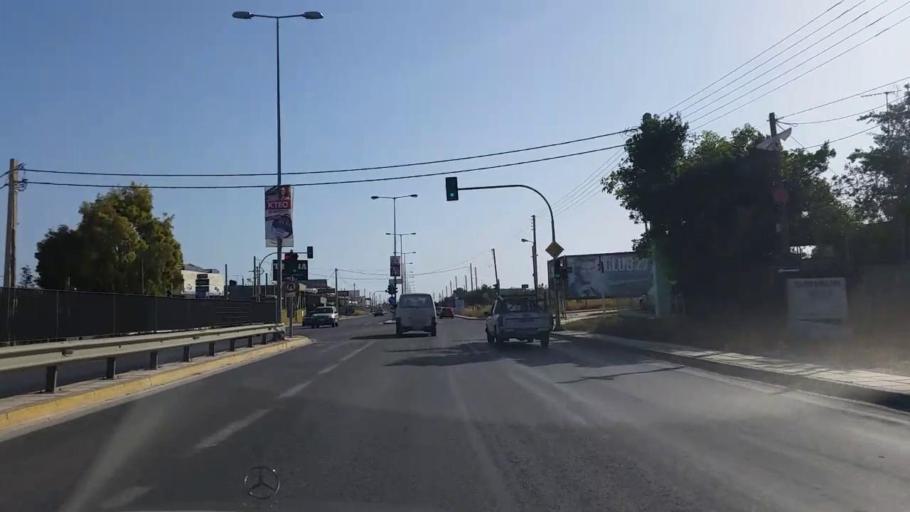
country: GR
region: Attica
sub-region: Nomarchia Anatolikis Attikis
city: Kitsi
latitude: 37.8716
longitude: 23.8583
